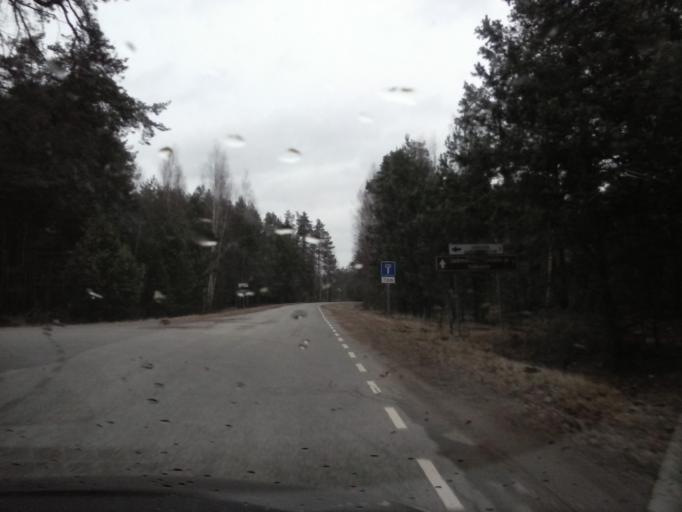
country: RU
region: Pskov
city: Pechory
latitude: 57.9620
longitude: 27.6304
